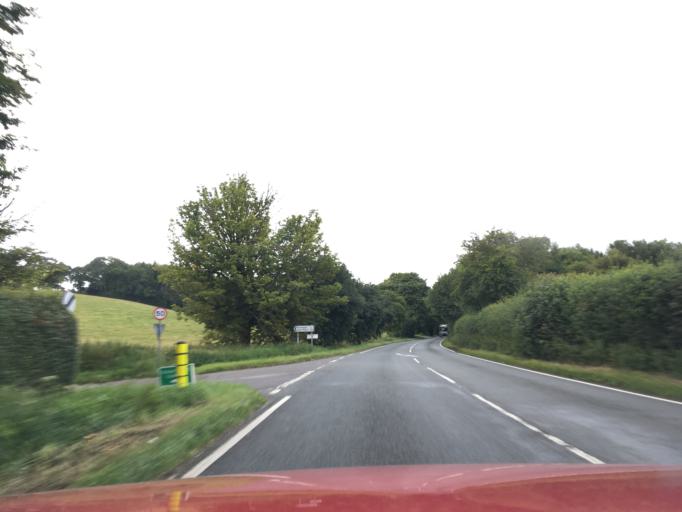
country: GB
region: England
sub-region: Hampshire
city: Four Marks
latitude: 51.0274
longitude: -1.0292
